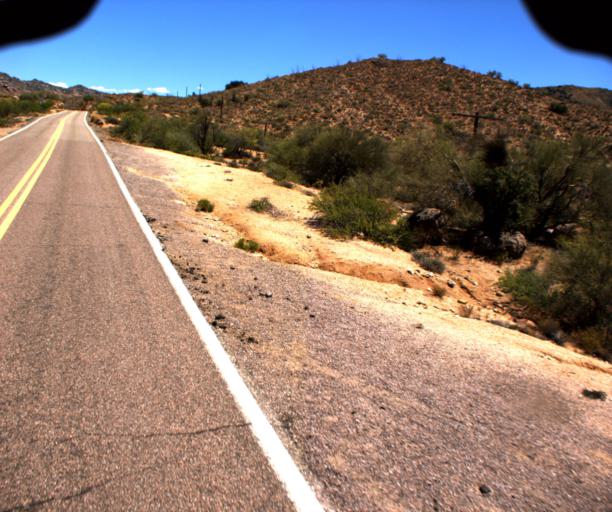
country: US
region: Arizona
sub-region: Yavapai County
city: Bagdad
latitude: 34.4537
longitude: -112.9923
